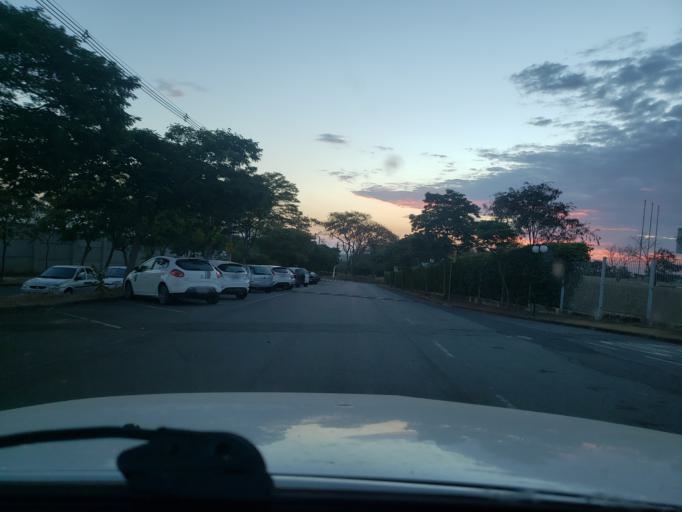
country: BR
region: Sao Paulo
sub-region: Mogi-Mirim
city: Mogi Mirim
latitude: -22.4892
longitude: -46.9795
